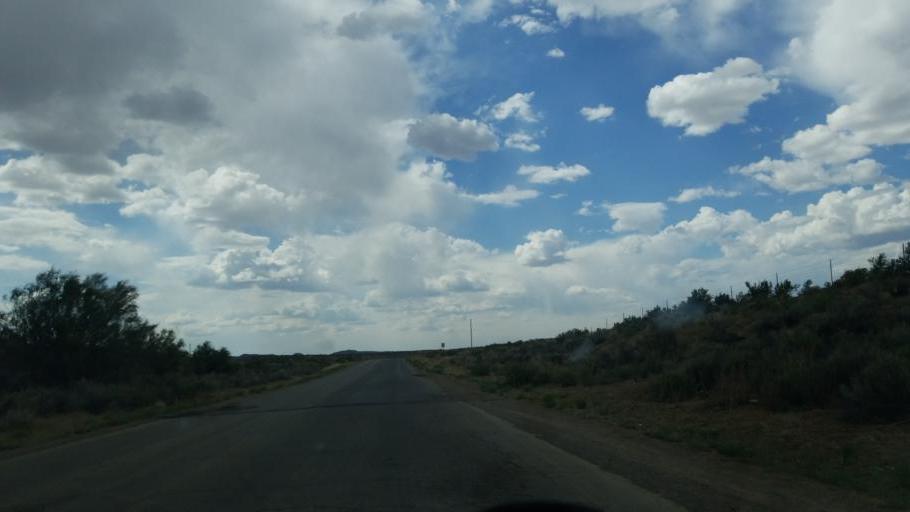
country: US
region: New Mexico
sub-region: McKinley County
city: Gallup
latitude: 35.4908
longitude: -108.9062
